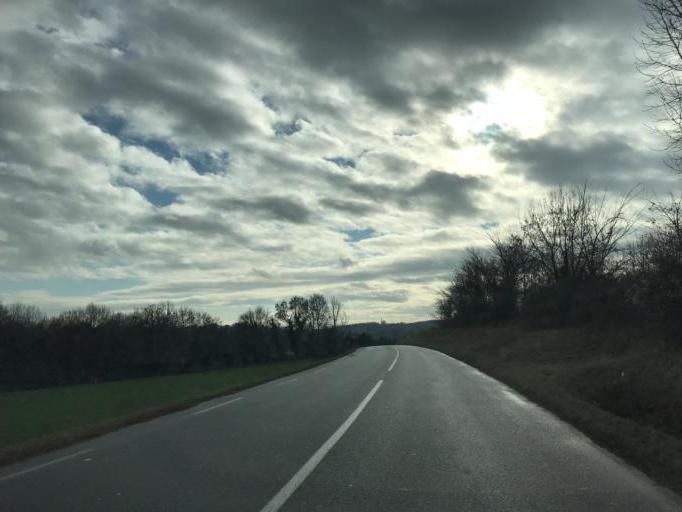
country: FR
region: Rhone-Alpes
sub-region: Departement de l'Ain
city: Sainte-Euphemie
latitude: 45.9773
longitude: 4.7982
